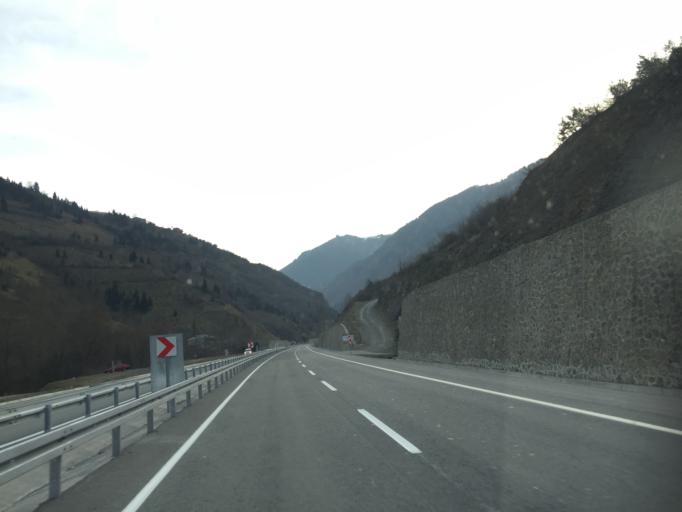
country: TR
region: Trabzon
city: Macka
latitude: 40.7895
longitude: 39.5797
